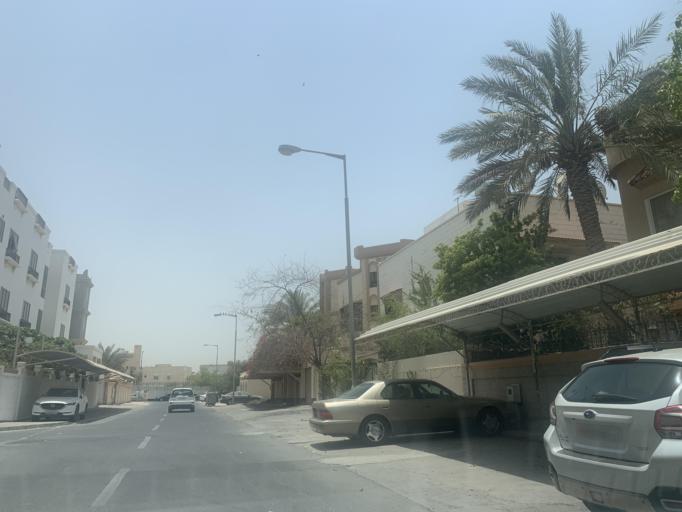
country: BH
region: Manama
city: Jidd Hafs
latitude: 26.2214
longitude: 50.4594
